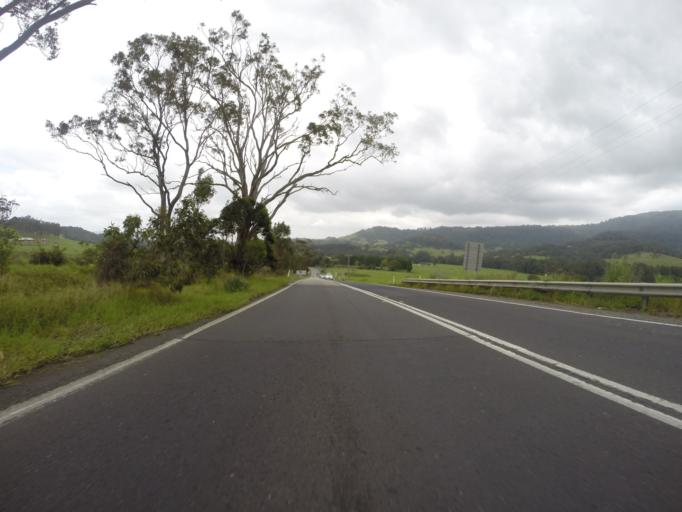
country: AU
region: New South Wales
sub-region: Kiama
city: Gerringong
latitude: -34.7394
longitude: 150.7681
